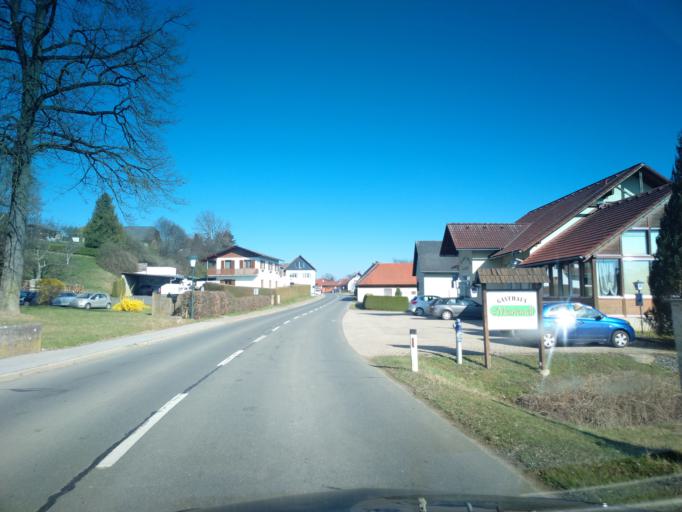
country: AT
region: Styria
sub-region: Politischer Bezirk Leibnitz
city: Weitendorf
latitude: 46.8967
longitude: 15.4606
